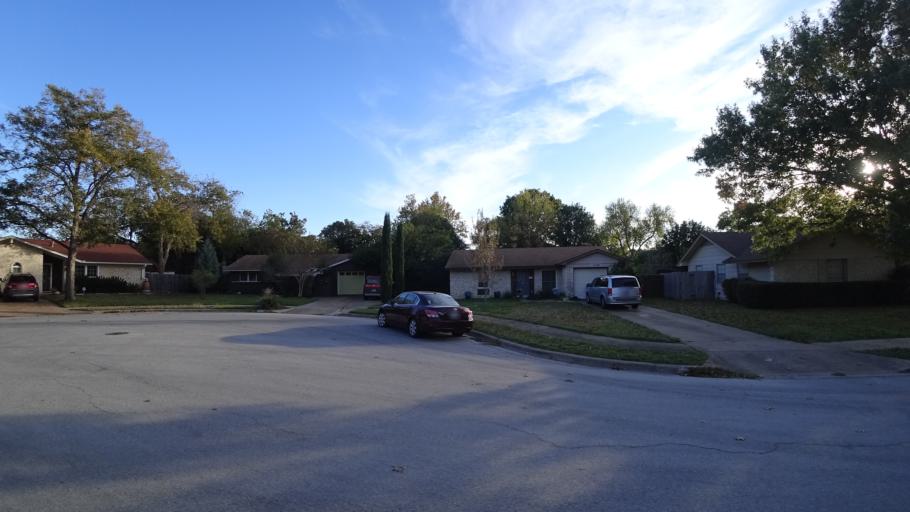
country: US
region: Texas
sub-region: Williamson County
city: Jollyville
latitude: 30.3677
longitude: -97.7354
